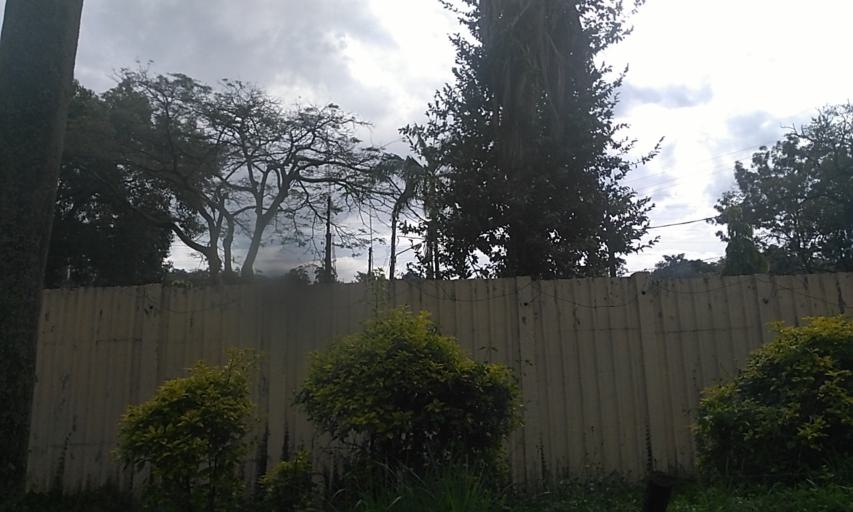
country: UG
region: Central Region
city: Kampala Central Division
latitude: 0.3341
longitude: 32.5863
